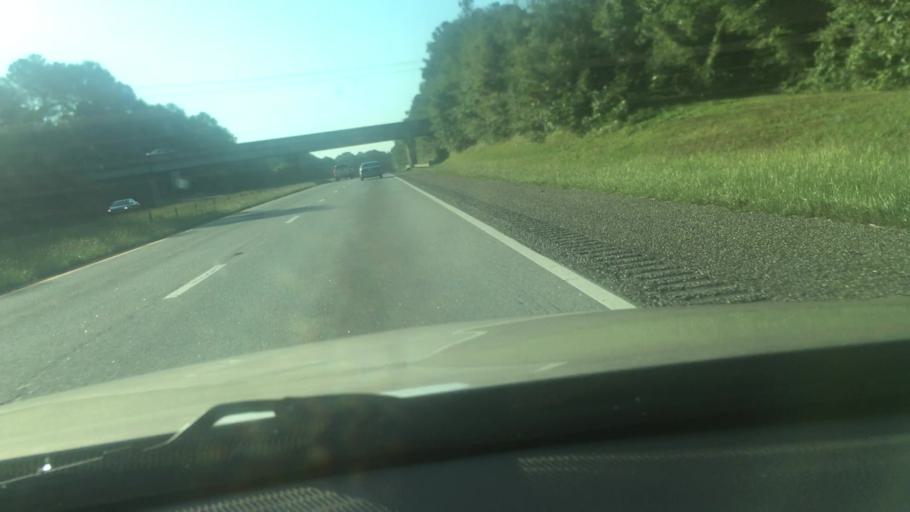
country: US
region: South Carolina
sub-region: Richland County
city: Lake Murray of Richland
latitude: 34.1370
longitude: -81.2185
